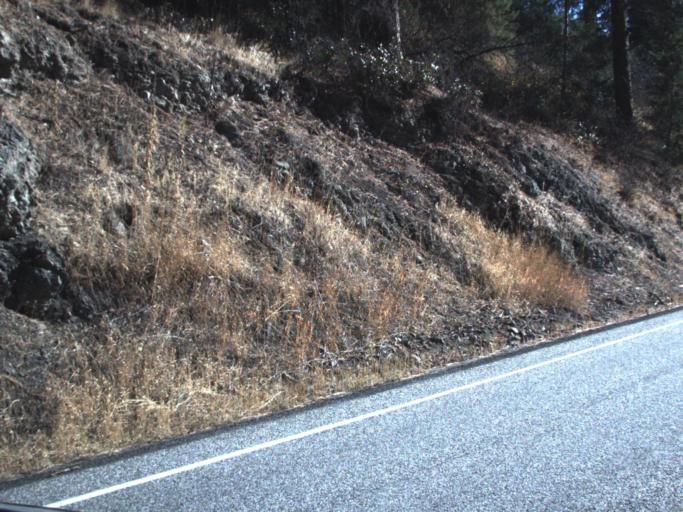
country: US
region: Washington
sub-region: Ferry County
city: Republic
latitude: 48.6385
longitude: -118.6791
